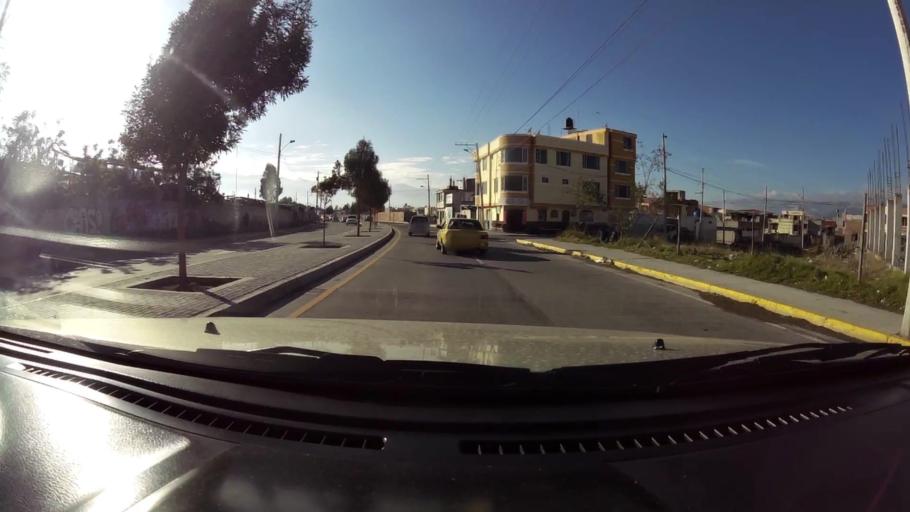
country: EC
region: Chimborazo
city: Riobamba
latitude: -1.6698
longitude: -78.6377
